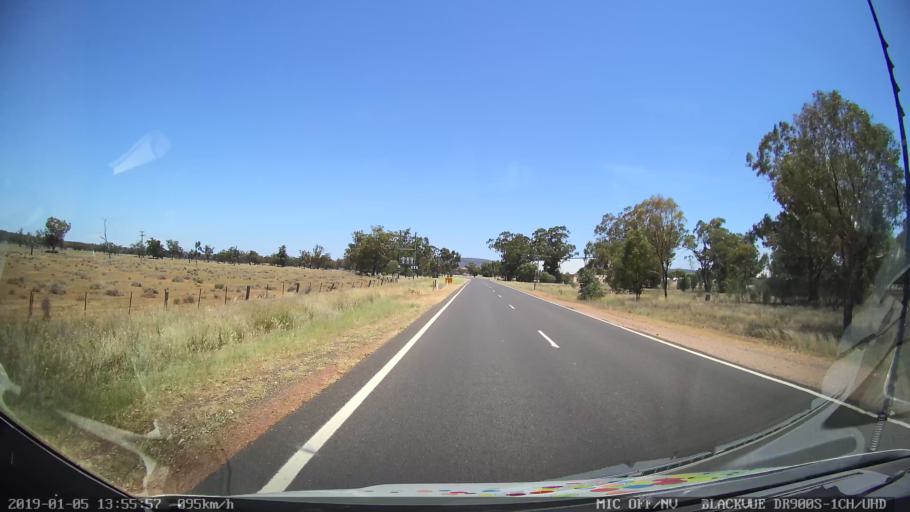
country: AU
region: New South Wales
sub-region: Gunnedah
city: Gunnedah
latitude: -31.1103
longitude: 150.2699
